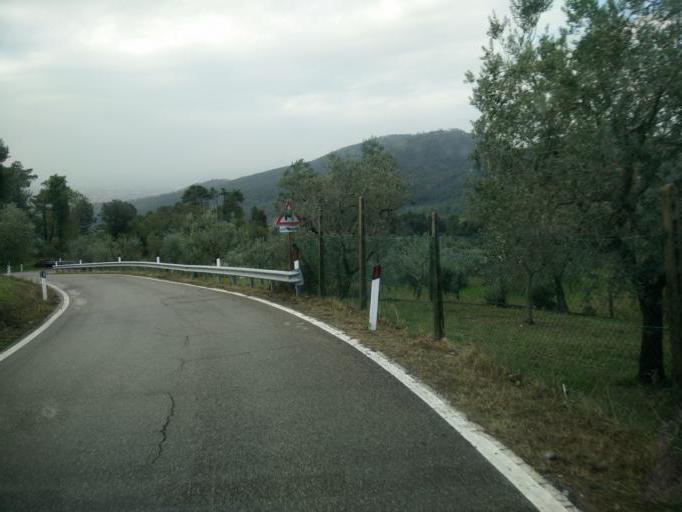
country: IT
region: Tuscany
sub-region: Provincia di Prato
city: Vaiano
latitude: 43.9367
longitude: 11.0963
